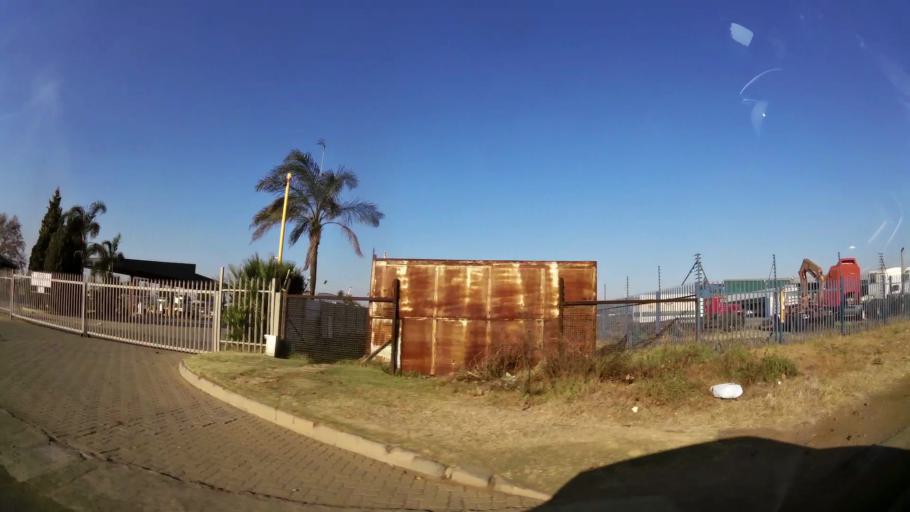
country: ZA
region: Gauteng
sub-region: West Rand District Municipality
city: Randfontein
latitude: -26.1989
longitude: 27.6967
